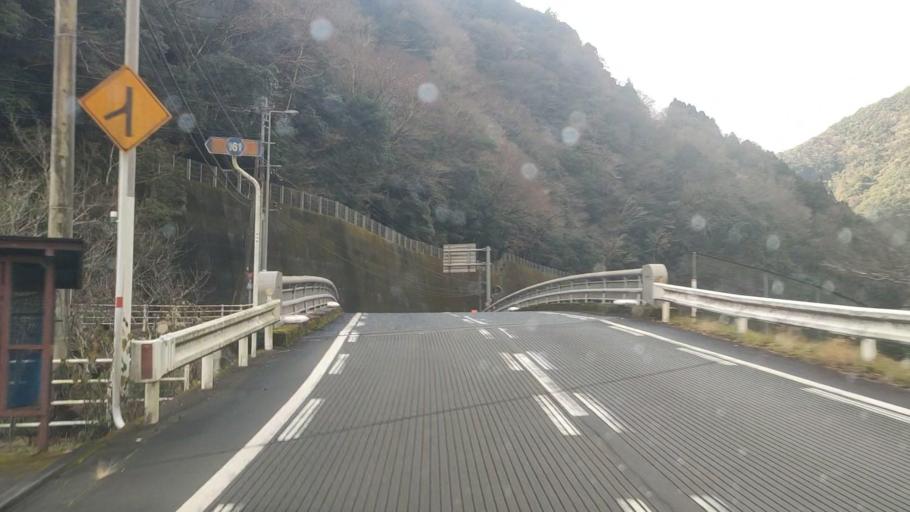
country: JP
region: Kumamoto
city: Hitoyoshi
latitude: 32.4187
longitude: 130.8529
